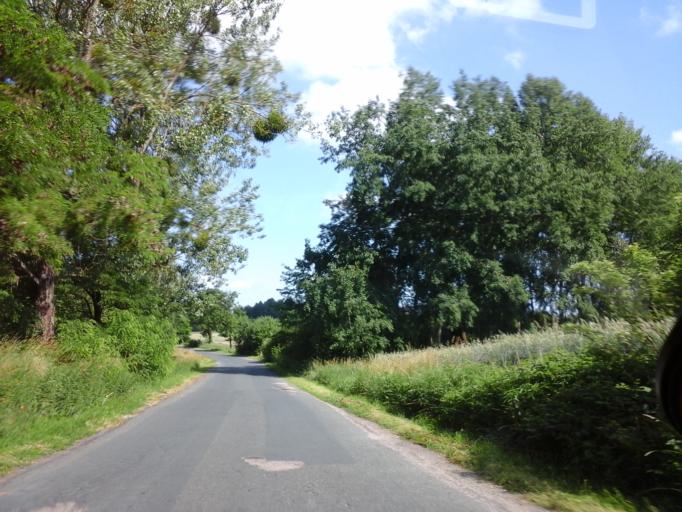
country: PL
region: West Pomeranian Voivodeship
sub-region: Powiat choszczenski
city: Recz
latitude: 53.2337
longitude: 15.5510
